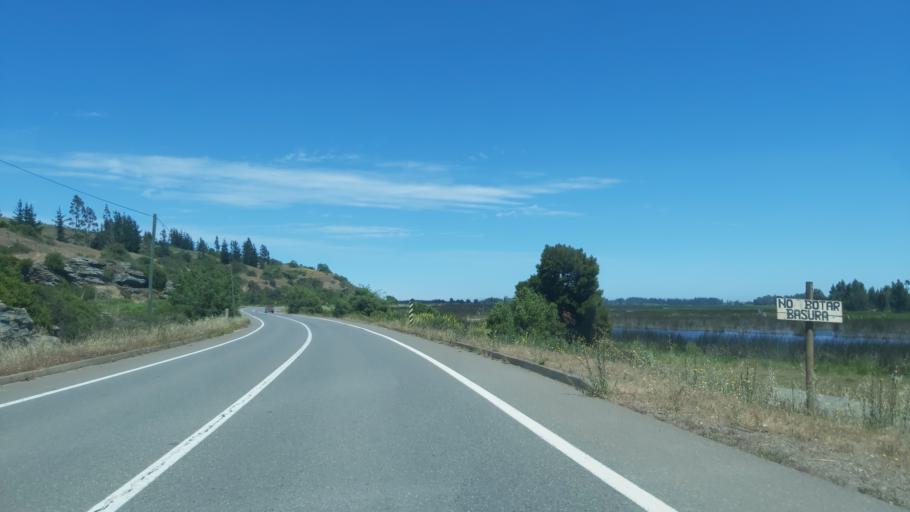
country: CL
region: Maule
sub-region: Provincia de Talca
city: Constitucion
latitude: -35.1548
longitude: -72.2452
